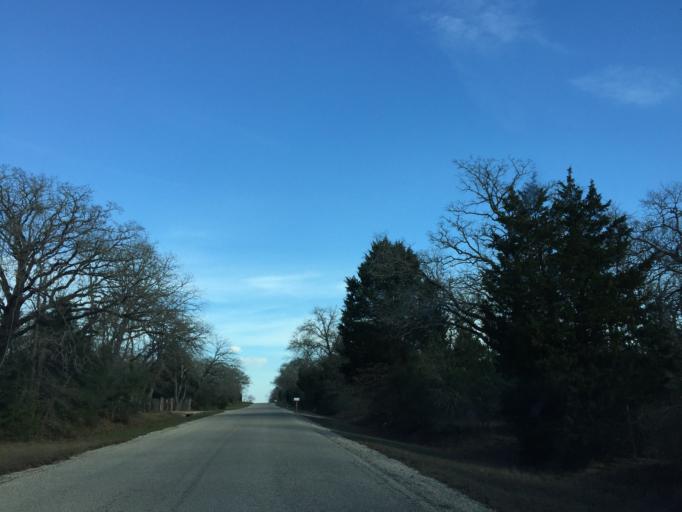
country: US
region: Texas
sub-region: Milam County
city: Thorndale
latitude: 30.4487
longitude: -97.2015
